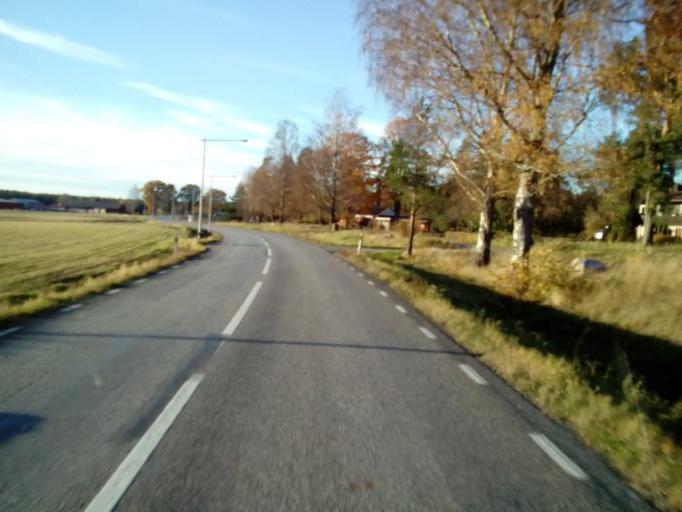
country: SE
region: OErebro
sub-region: Hallsbergs Kommun
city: Palsboda
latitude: 59.0233
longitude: 15.3762
